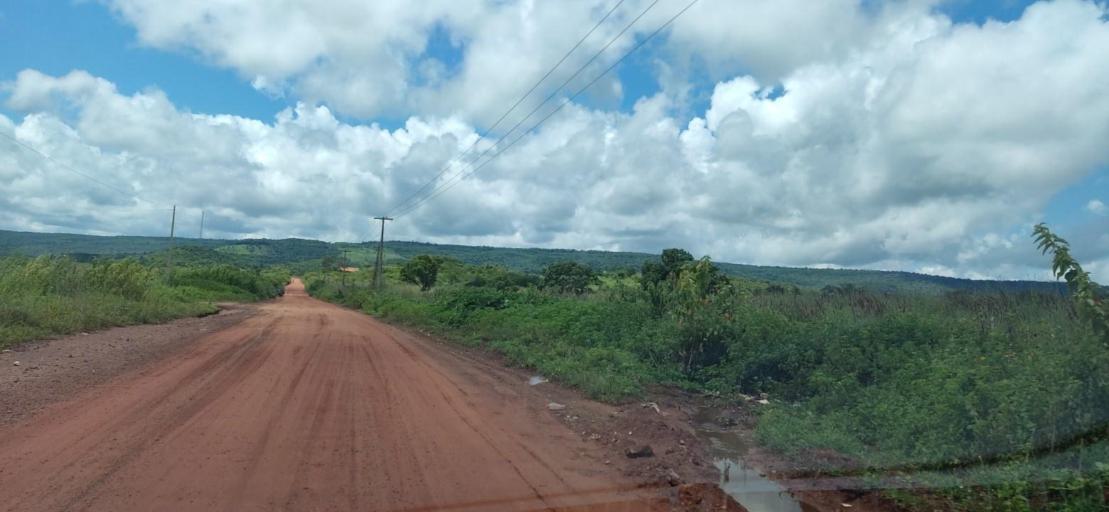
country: BR
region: Piaui
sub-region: Valenca Do Piaui
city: Valenca do Piaui
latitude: -6.1054
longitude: -41.8150
